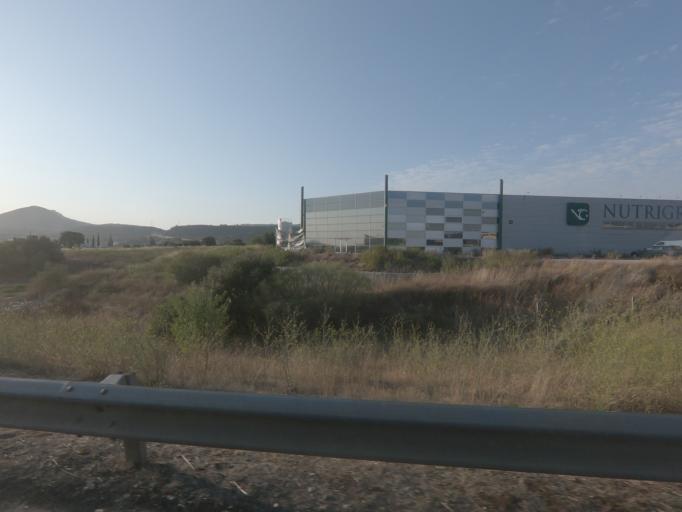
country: PT
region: Santarem
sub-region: Alcanena
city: Alcanena
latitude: 39.4776
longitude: -8.6301
